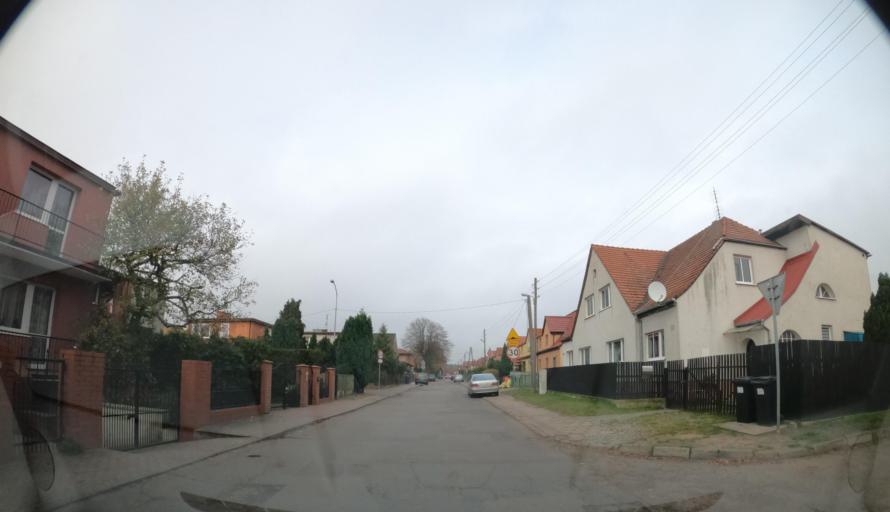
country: PL
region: West Pomeranian Voivodeship
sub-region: Powiat goleniowski
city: Goleniow
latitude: 53.5709
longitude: 14.8366
